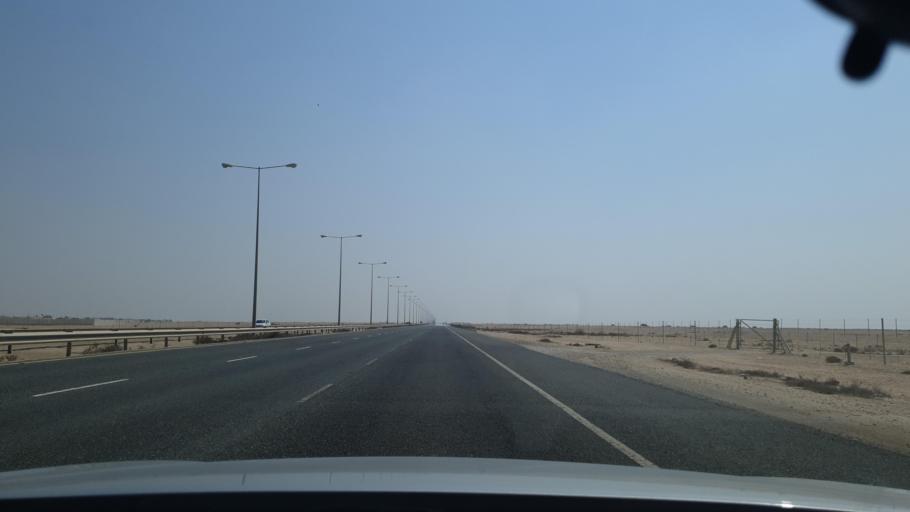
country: QA
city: Al Ghuwayriyah
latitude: 25.8099
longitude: 51.3747
